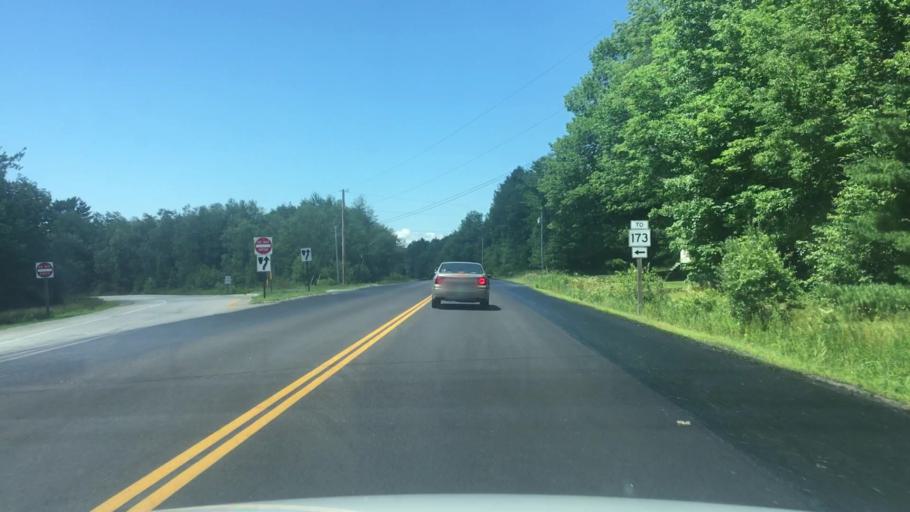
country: US
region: Maine
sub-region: Waldo County
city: Searsmont
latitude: 44.4023
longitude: -69.2692
